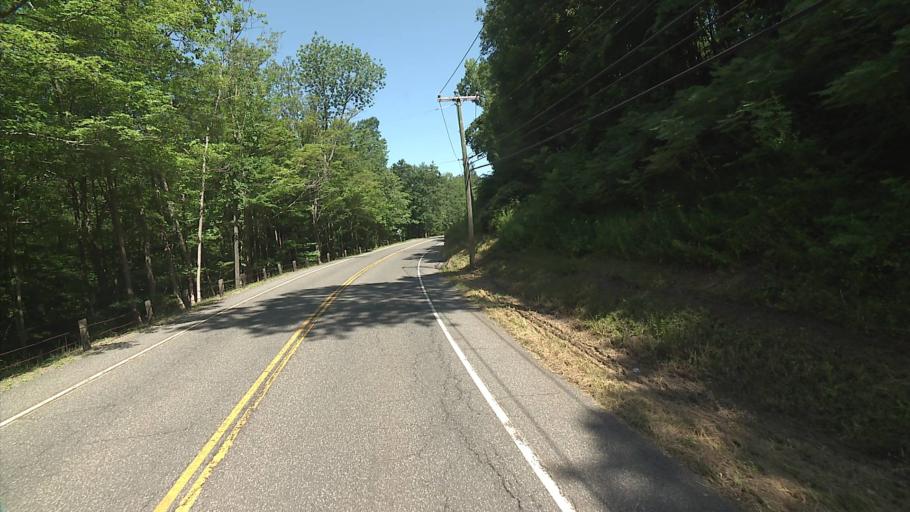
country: US
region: Connecticut
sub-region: Litchfield County
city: New Preston
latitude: 41.7078
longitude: -73.3455
